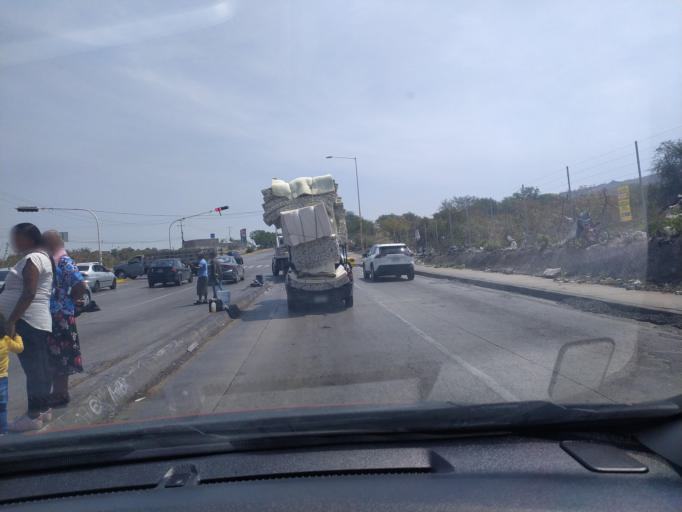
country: MX
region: Jalisco
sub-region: Tlajomulco de Zuniga
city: Altus Bosques
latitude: 20.5917
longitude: -103.3811
